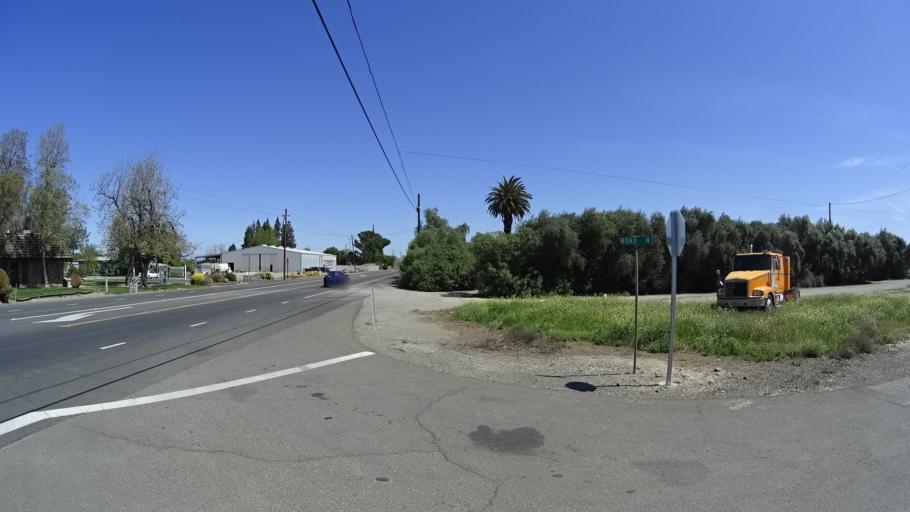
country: US
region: California
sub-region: Glenn County
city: Orland
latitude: 39.7469
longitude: -122.1598
